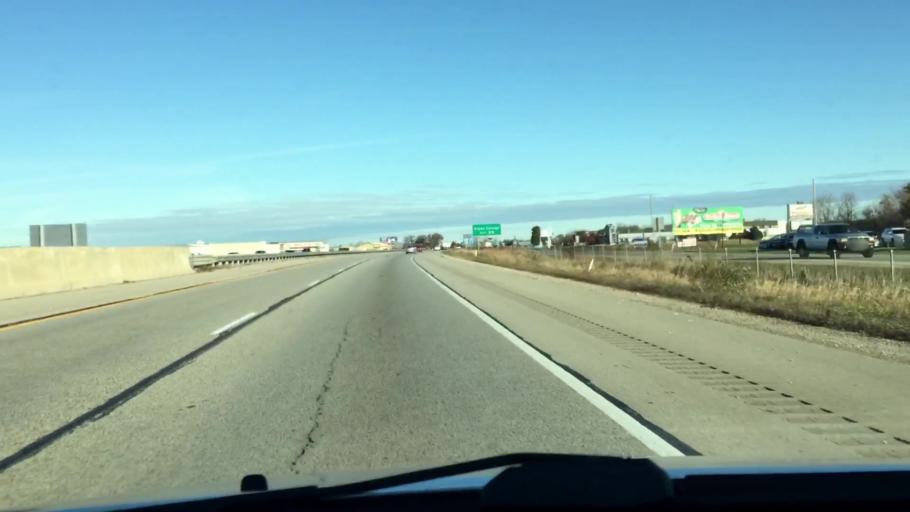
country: US
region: Wisconsin
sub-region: Fond du Lac County
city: North Fond du Lac
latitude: 43.7689
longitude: -88.4813
